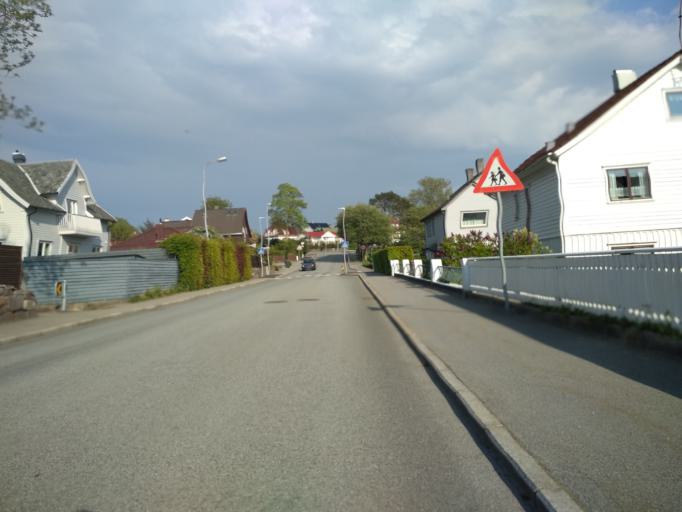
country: NO
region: Rogaland
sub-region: Stavanger
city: Stavanger
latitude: 58.9690
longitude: 5.7092
